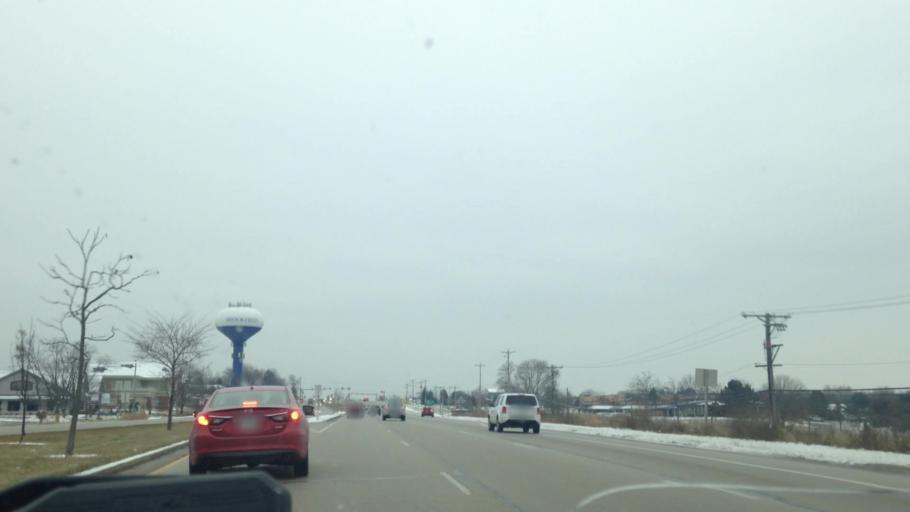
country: US
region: Wisconsin
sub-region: Waukesha County
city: Brookfield
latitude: 43.0903
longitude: -88.1330
